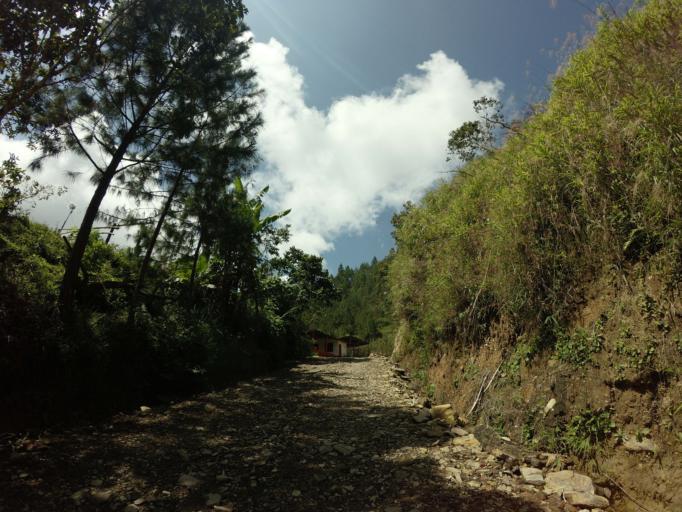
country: CO
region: Caldas
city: Pensilvania
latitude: 5.4805
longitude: -75.1814
